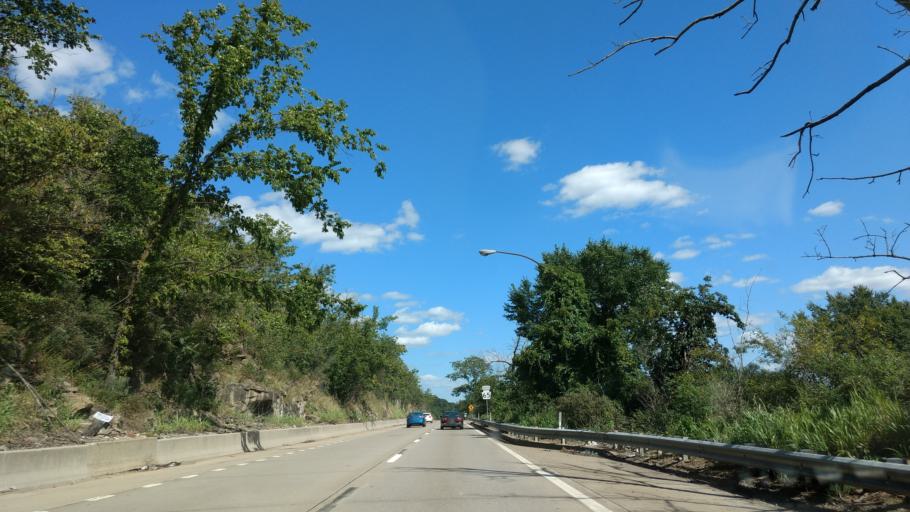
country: US
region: Pennsylvania
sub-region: Allegheny County
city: Emsworth
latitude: 40.5164
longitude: -80.1244
